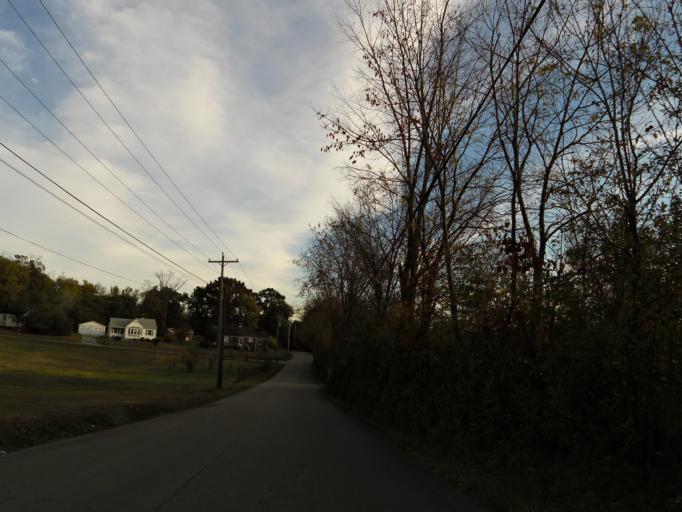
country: US
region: Tennessee
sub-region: Blount County
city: Alcoa
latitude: 35.7837
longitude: -83.9544
